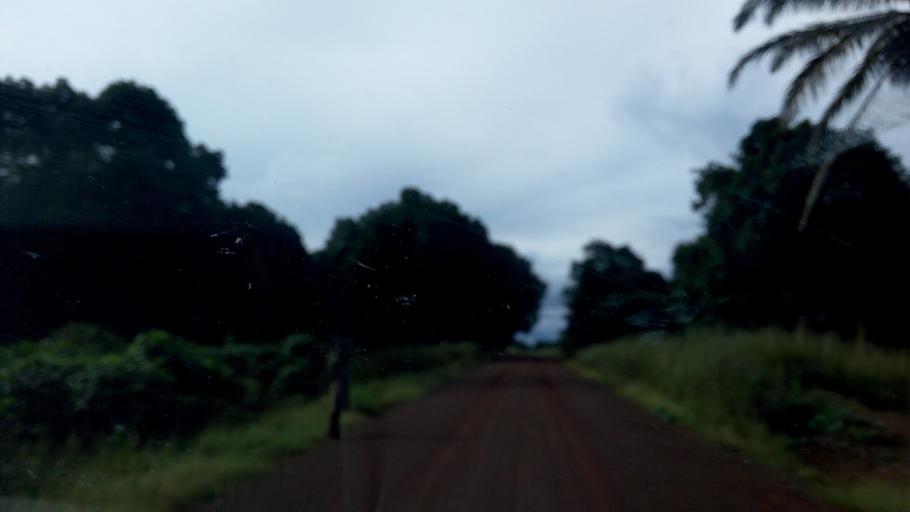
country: ZM
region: Luapula
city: Mwense
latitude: -10.3976
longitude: 28.1152
